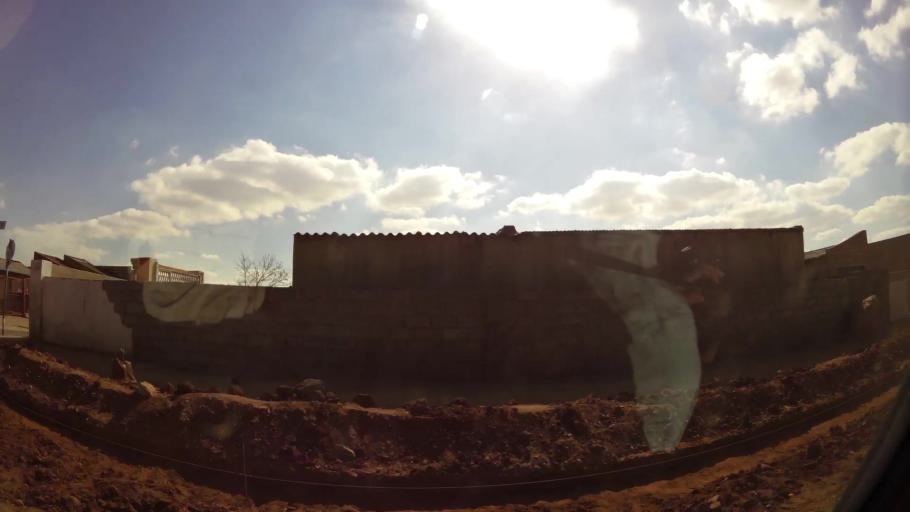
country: ZA
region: Gauteng
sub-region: Ekurhuleni Metropolitan Municipality
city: Tembisa
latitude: -26.0029
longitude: 28.2183
